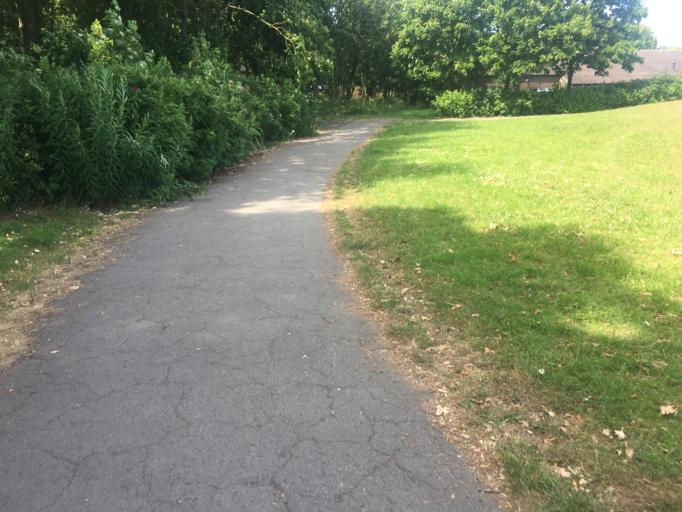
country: GB
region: England
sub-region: County Durham
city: Chester-le-Street
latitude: 54.8785
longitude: -1.5494
